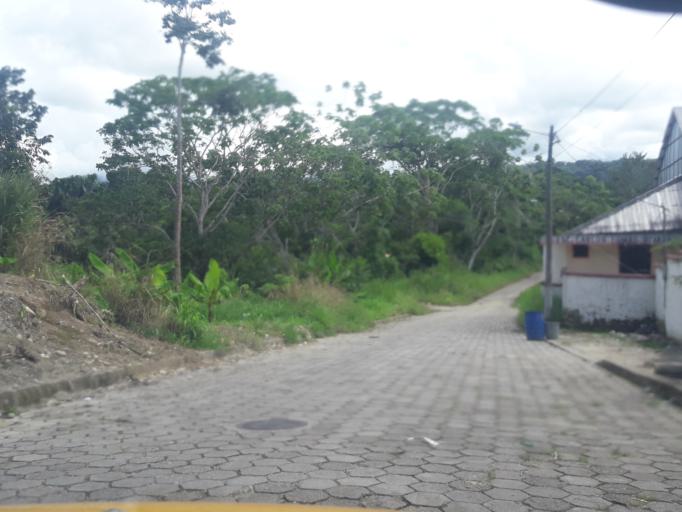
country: EC
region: Napo
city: Tena
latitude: -1.0070
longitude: -77.8216
